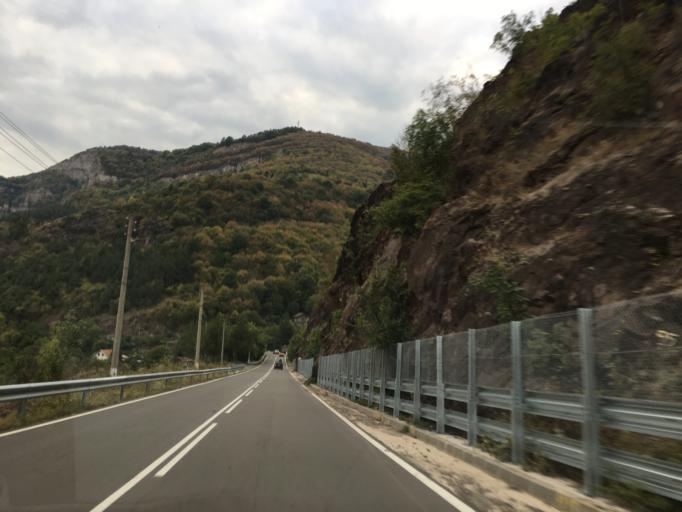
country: BG
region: Sofiya
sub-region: Obshtina Svoge
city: Bov
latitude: 43.0300
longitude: 23.3513
